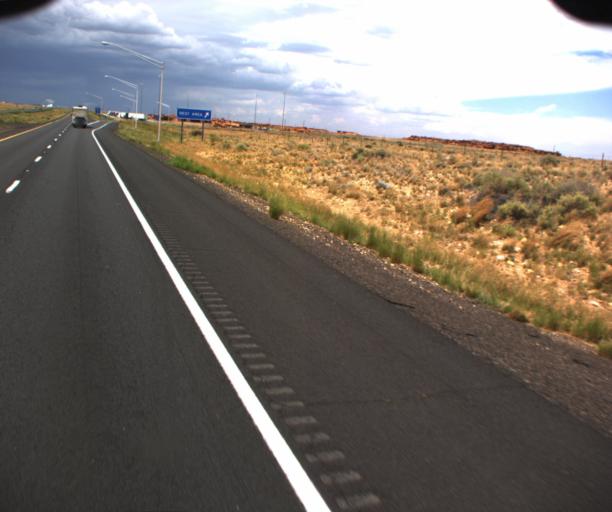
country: US
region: Arizona
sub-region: Coconino County
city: LeChee
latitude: 35.1018
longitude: -110.9870
